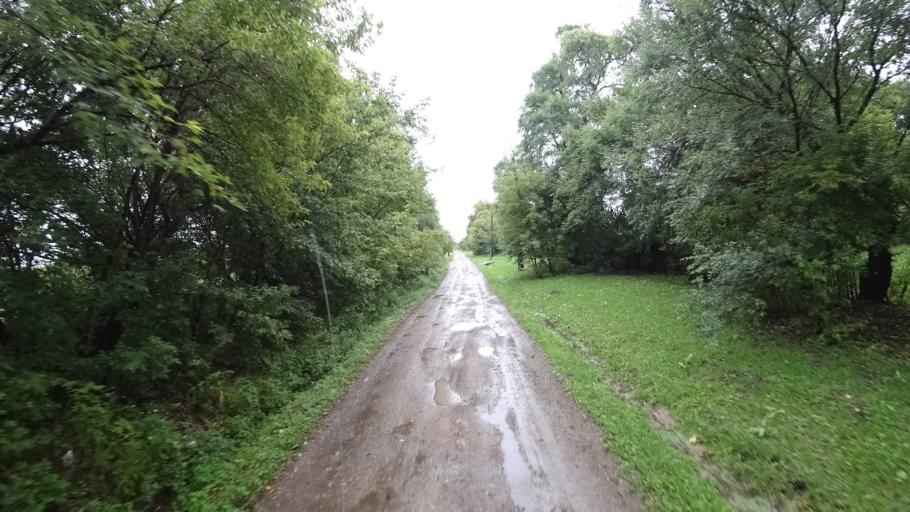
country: RU
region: Primorskiy
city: Monastyrishche
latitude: 44.2531
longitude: 132.4239
